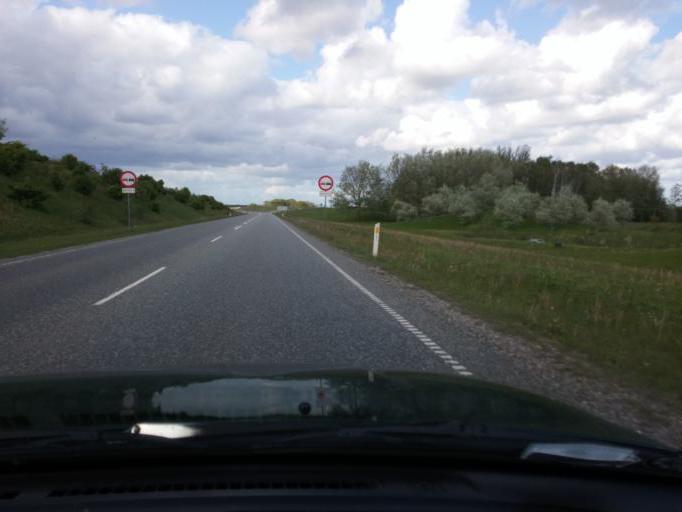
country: DK
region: South Denmark
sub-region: Odense Kommune
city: Neder Holluf
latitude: 55.3697
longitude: 10.4731
